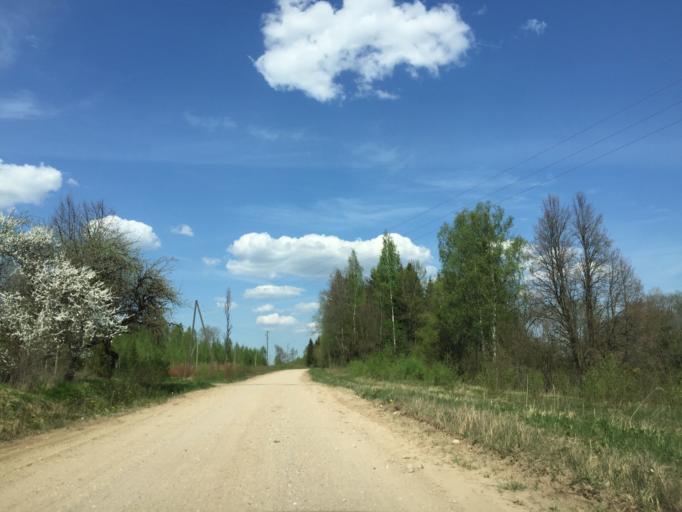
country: LV
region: Limbazu Rajons
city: Limbazi
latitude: 57.3653
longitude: 24.6368
